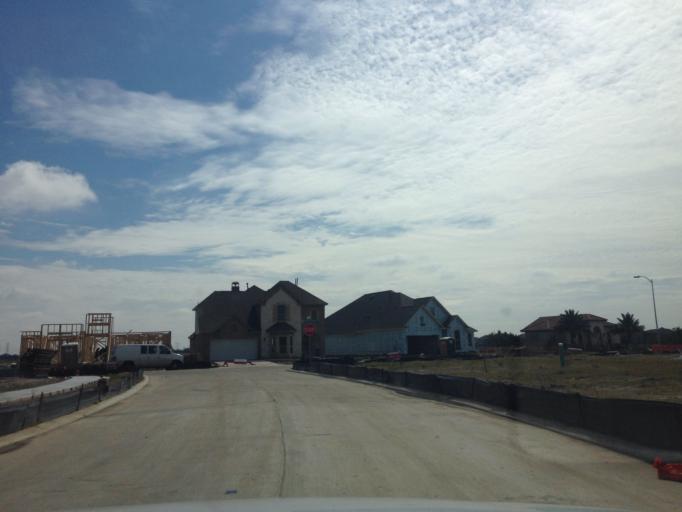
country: US
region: Texas
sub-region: Galveston County
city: Kemah
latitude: 29.5187
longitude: -95.0150
